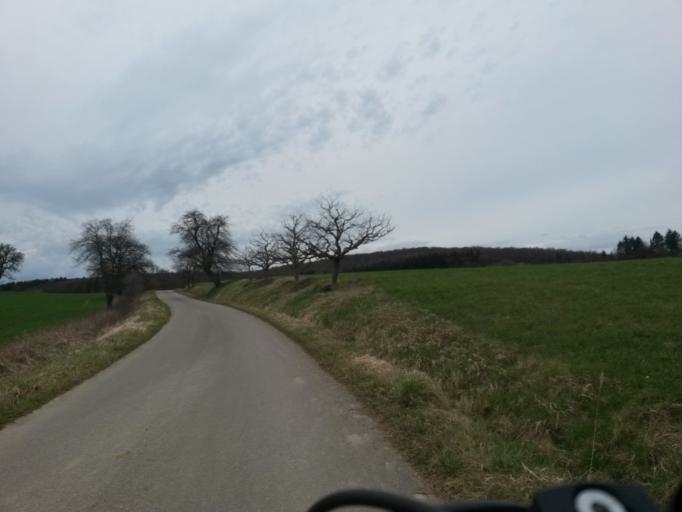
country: DE
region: Baden-Wuerttemberg
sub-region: Karlsruhe Region
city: Neuenburg
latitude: 48.9040
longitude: 8.5598
